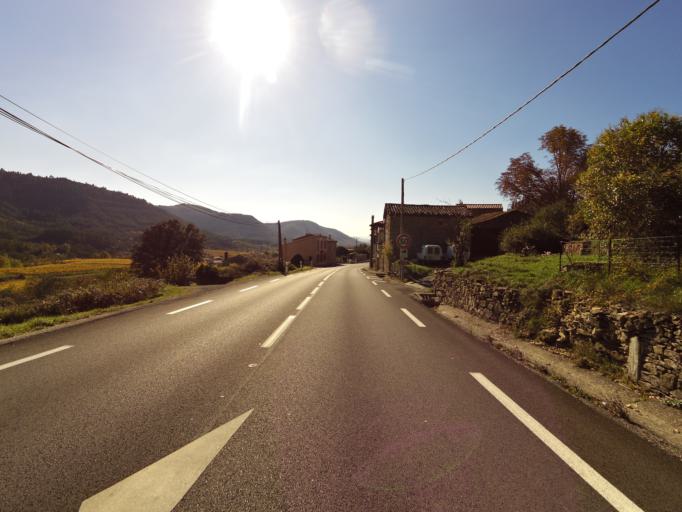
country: FR
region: Rhone-Alpes
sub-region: Departement de l'Ardeche
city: Vesseaux
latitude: 44.6693
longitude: 4.4559
